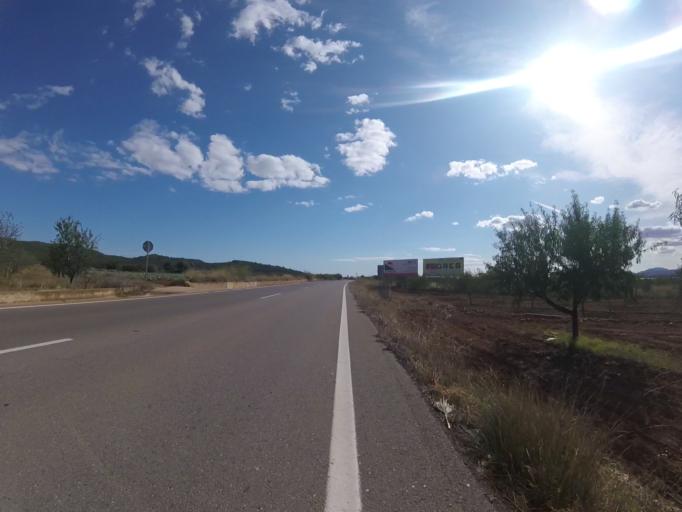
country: ES
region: Valencia
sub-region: Provincia de Castello
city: Alcala de Xivert
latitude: 40.2617
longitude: 0.2434
